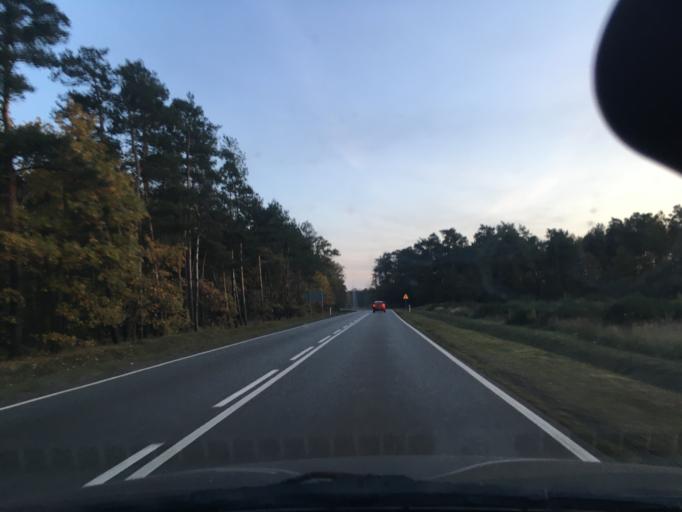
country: PL
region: Masovian Voivodeship
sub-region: Powiat sochaczewski
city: Mlodzieszyn
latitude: 52.3383
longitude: 20.2143
